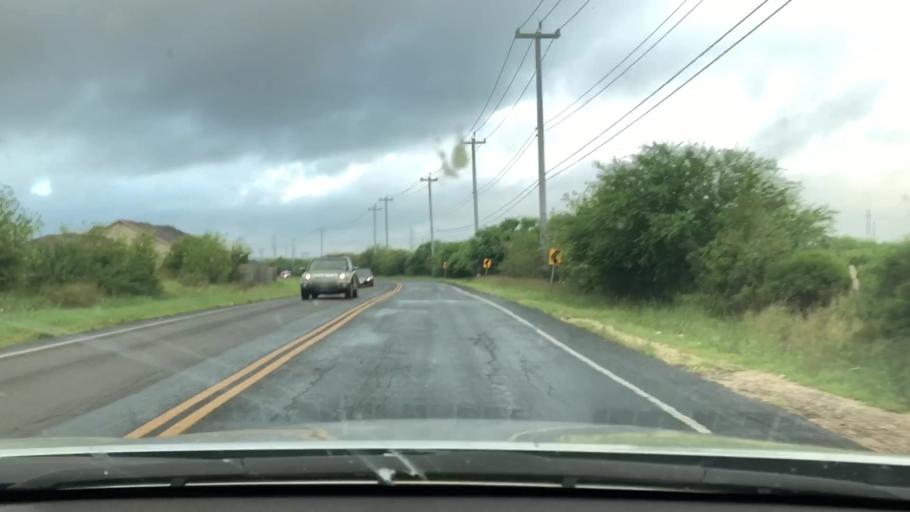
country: US
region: Texas
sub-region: Bexar County
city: Converse
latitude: 29.4764
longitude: -98.3150
